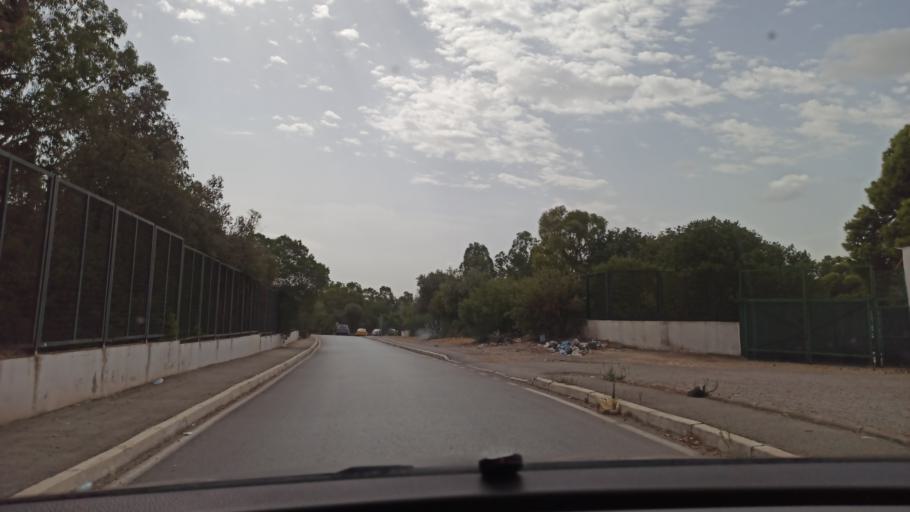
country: TN
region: Tunis
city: Tunis
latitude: 36.8209
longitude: 10.1681
